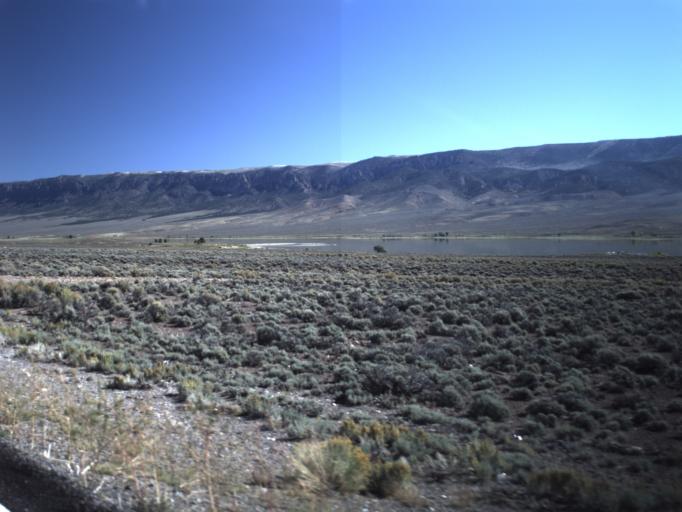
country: US
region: Utah
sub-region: Piute County
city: Junction
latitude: 38.1936
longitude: -112.0110
